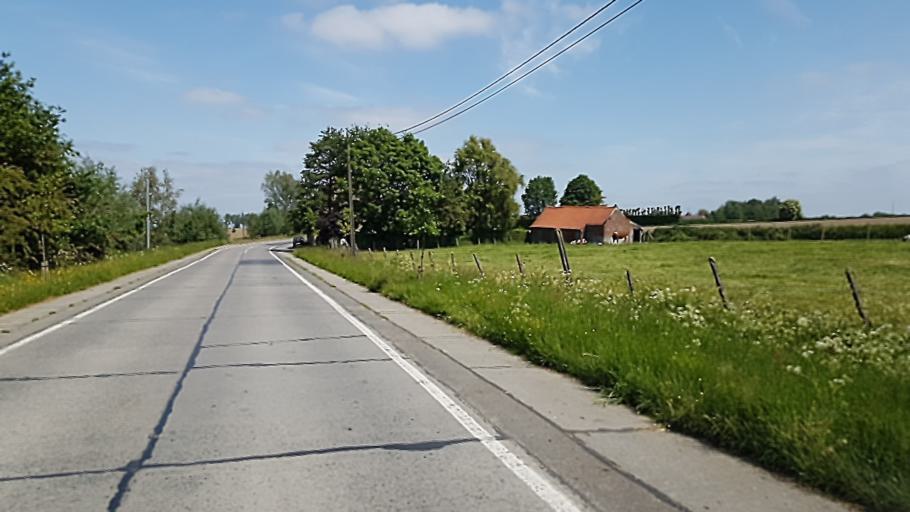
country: BE
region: Flanders
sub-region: Provincie West-Vlaanderen
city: Anzegem
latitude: 50.8252
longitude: 3.4436
